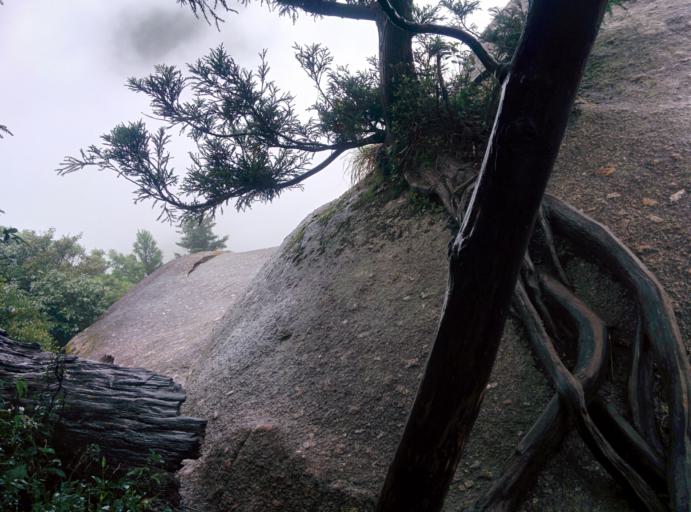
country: JP
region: Kagoshima
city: Nishinoomote
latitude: 30.3624
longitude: 130.5683
